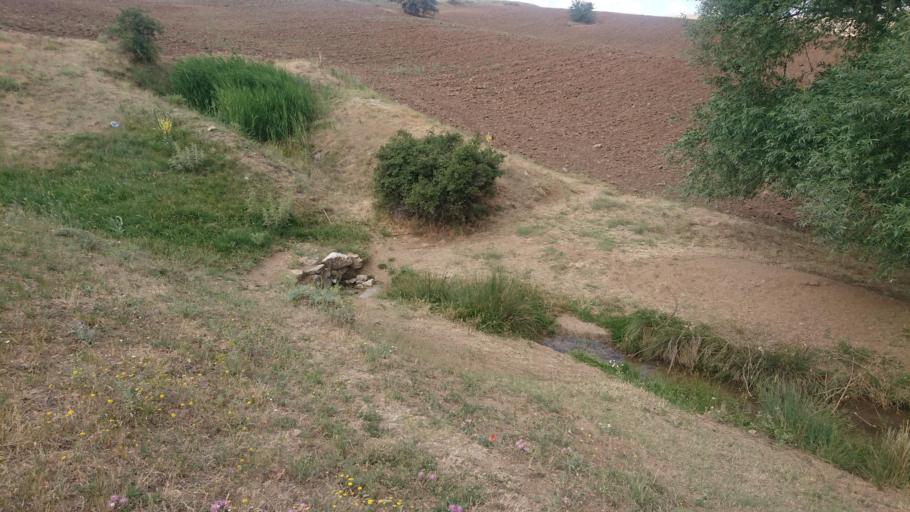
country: TR
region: Aksaray
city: Agacoren
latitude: 38.8420
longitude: 33.9377
